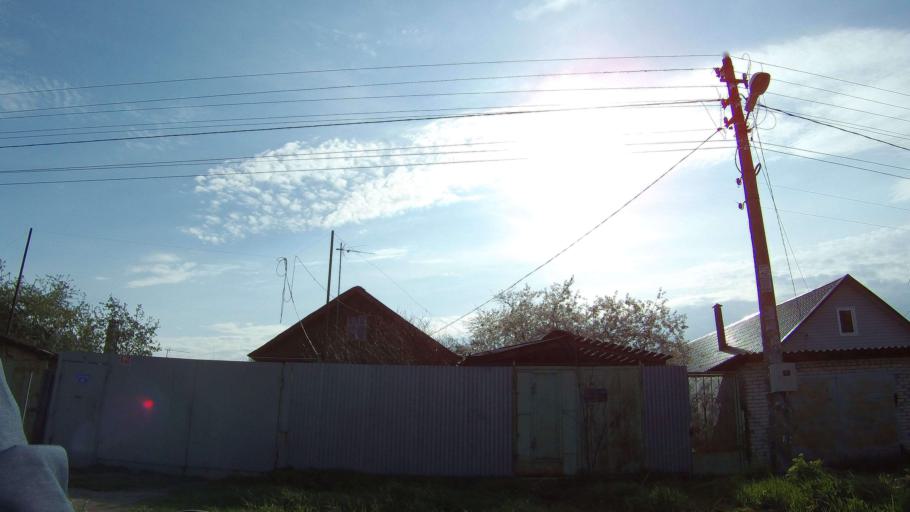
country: RU
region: Moskovskaya
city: Ramenskoye
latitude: 55.5588
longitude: 38.2327
